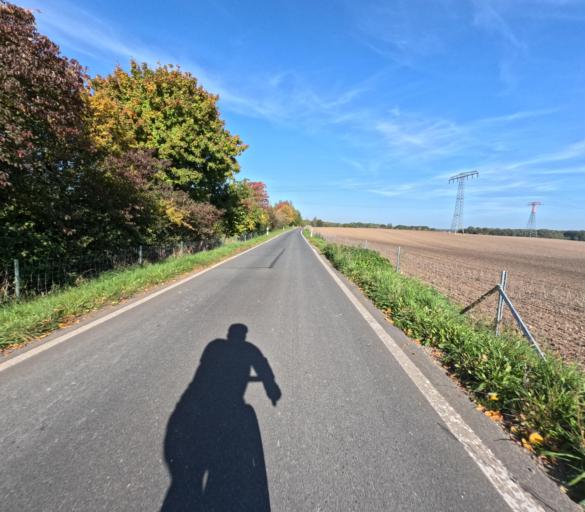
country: DE
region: Saxony
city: Ottendorf-Okrilla
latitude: 51.1542
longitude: 13.7873
